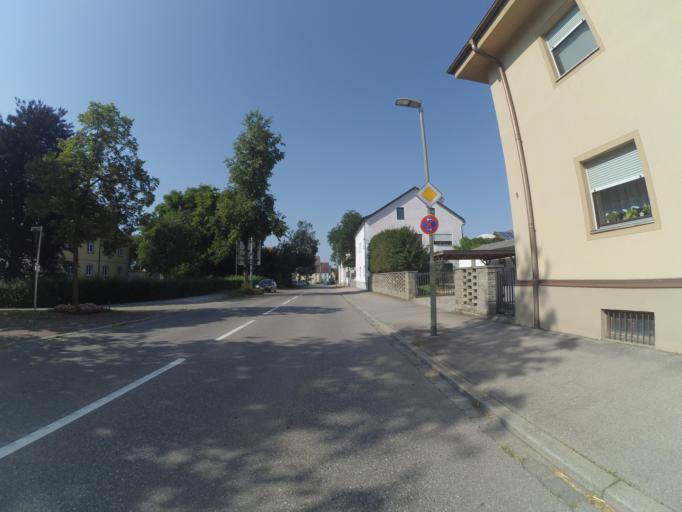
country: DE
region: Bavaria
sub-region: Swabia
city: Buchloe
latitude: 48.0381
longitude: 10.7299
